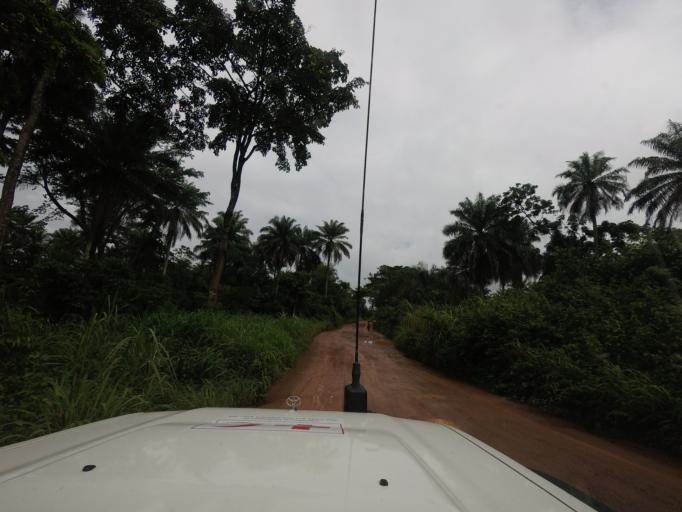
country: GN
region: Nzerekore
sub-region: Nzerekore Prefecture
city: Nzerekore
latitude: 7.7268
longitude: -8.8627
